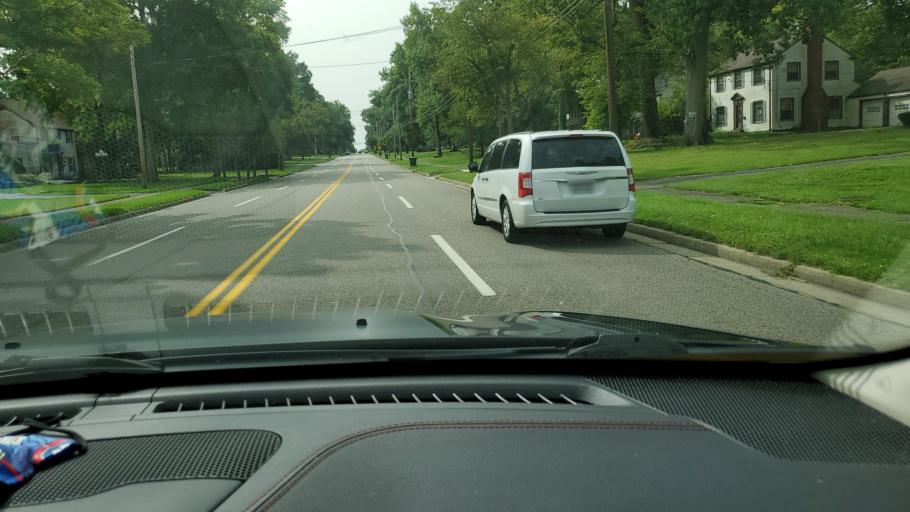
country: US
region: Ohio
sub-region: Mahoning County
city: Boardman
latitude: 41.0383
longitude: -80.6723
